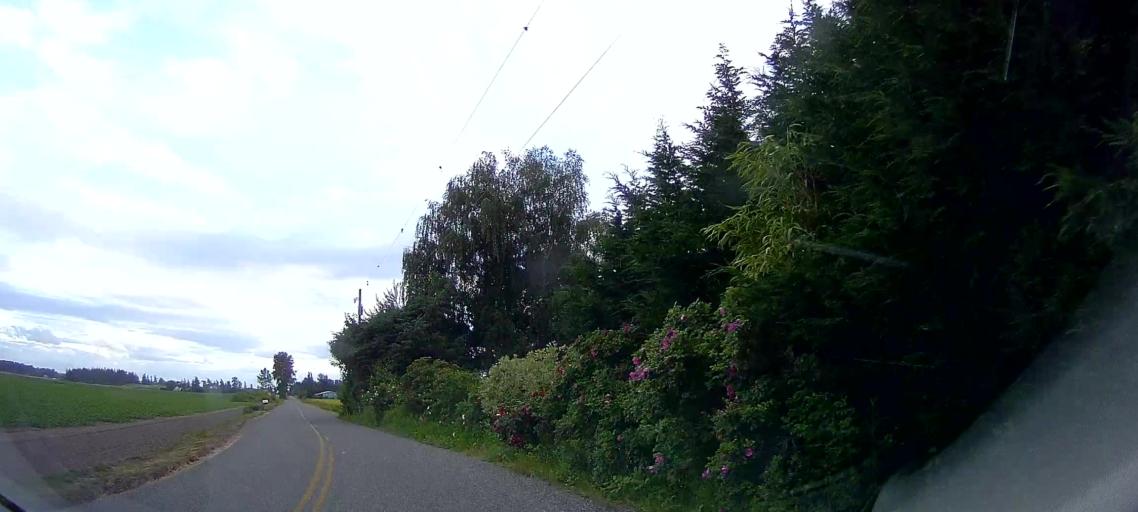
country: US
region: Washington
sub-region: Skagit County
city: Mount Vernon
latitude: 48.3794
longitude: -122.3790
